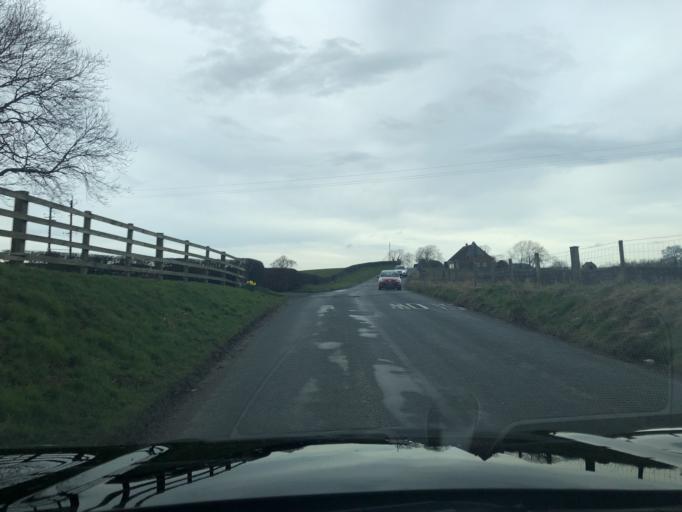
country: GB
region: England
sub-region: North Yorkshire
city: Northallerton
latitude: 54.3383
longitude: -1.4519
